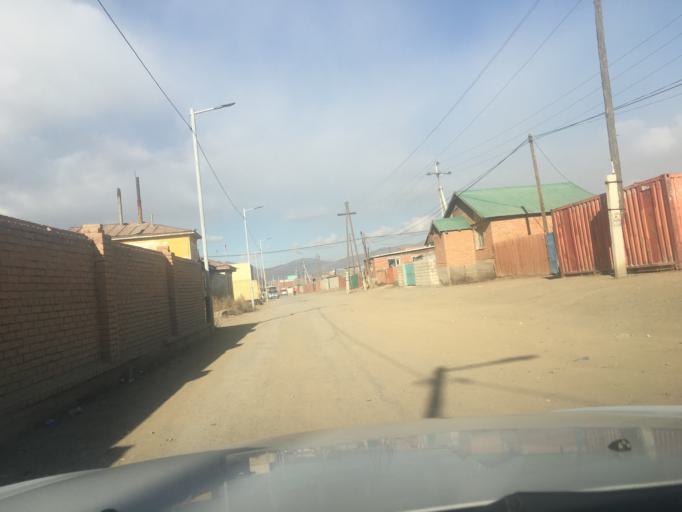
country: MN
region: Ulaanbaatar
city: Ulaanbaatar
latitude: 47.9446
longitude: 106.8253
